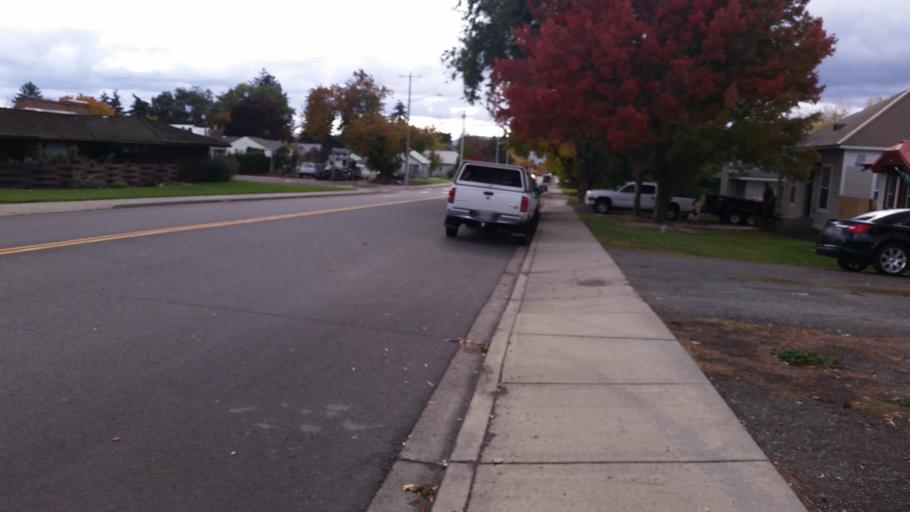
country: US
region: Washington
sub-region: Kittitas County
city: Ellensburg
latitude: 46.9932
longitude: -120.5372
